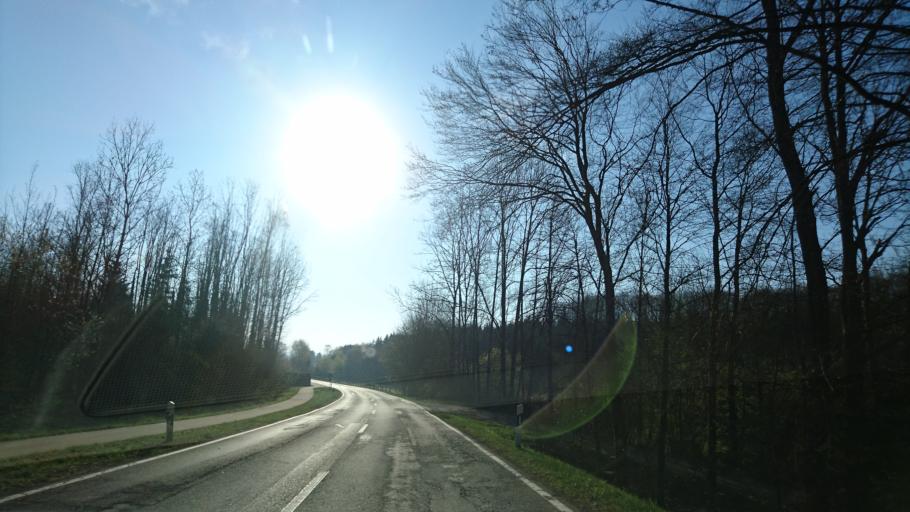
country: DE
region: Bavaria
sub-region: Swabia
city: Gablingen
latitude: 48.4409
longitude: 10.7914
